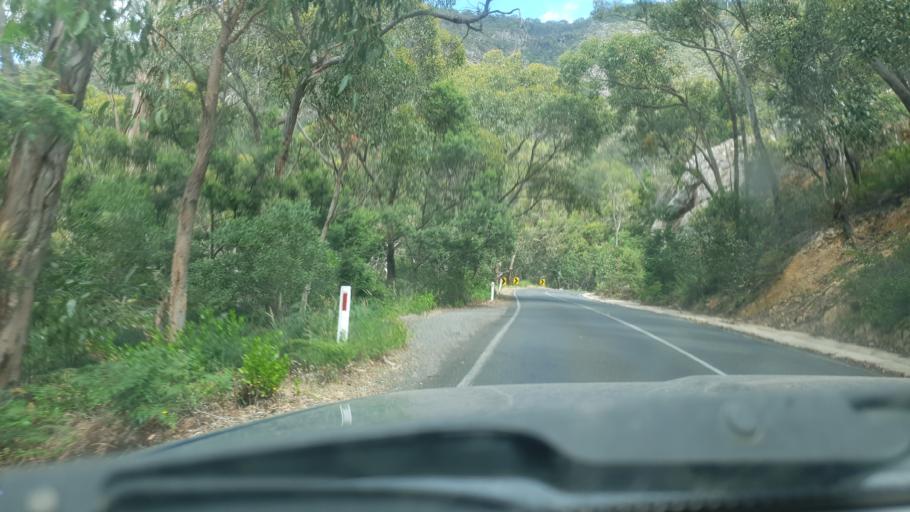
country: AU
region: Victoria
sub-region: Northern Grampians
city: Stawell
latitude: -37.1370
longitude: 142.5131
